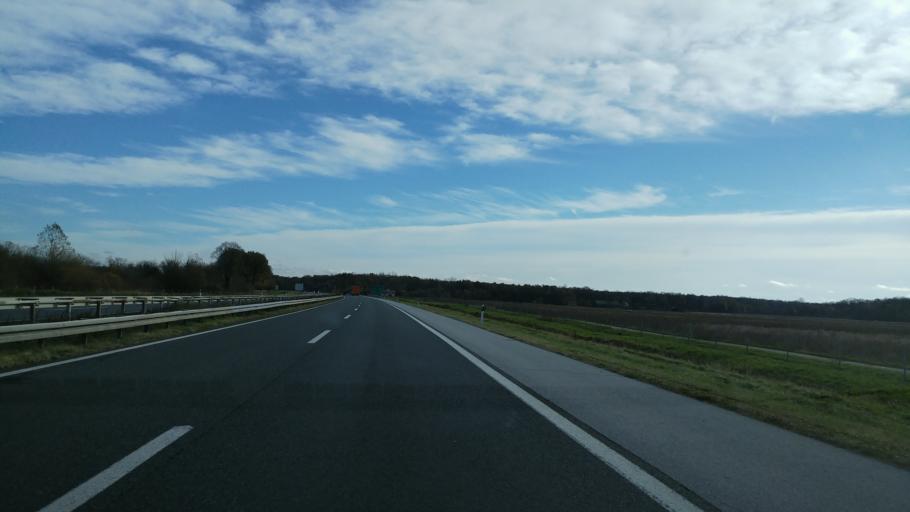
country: HR
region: Sisacko-Moslavacka
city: Kutina
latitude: 45.4556
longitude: 16.7667
